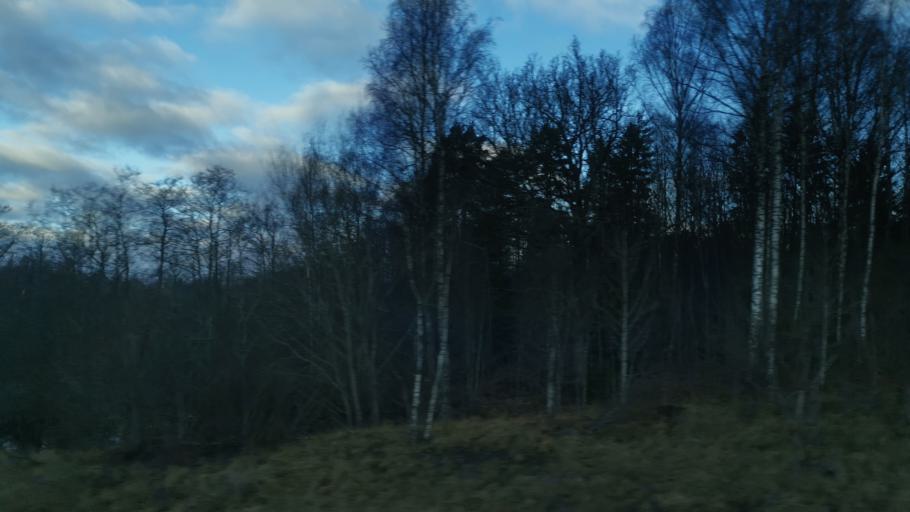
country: SE
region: Soedermanland
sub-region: Flens Kommun
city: Flen
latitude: 59.0598
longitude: 16.5998
